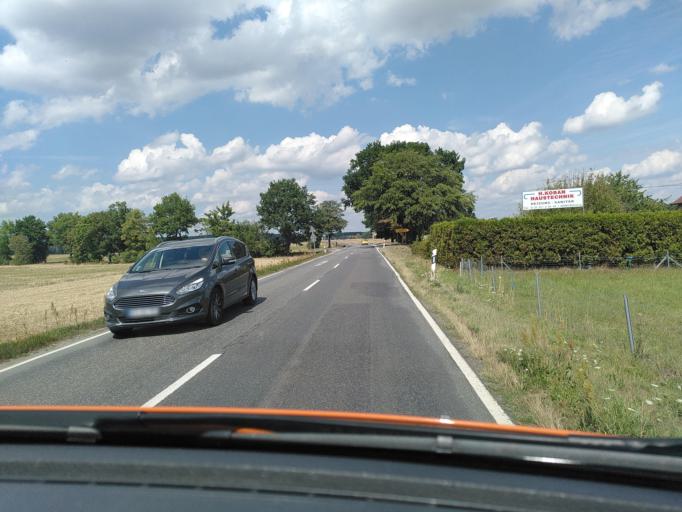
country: DE
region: Saxony
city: Grossdubrau
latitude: 51.2372
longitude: 14.4830
